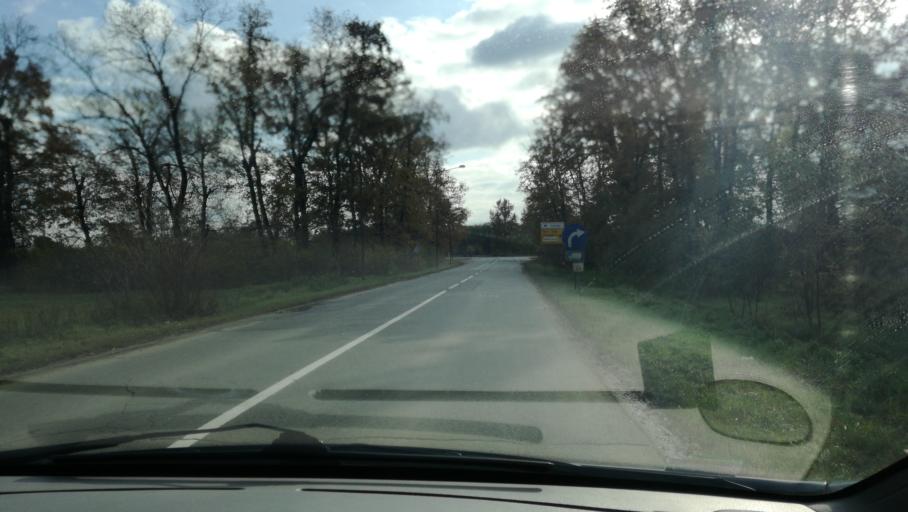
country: RS
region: Autonomna Pokrajina Vojvodina
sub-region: Severnobanatski Okrug
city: Kikinda
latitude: 45.8195
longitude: 20.4417
